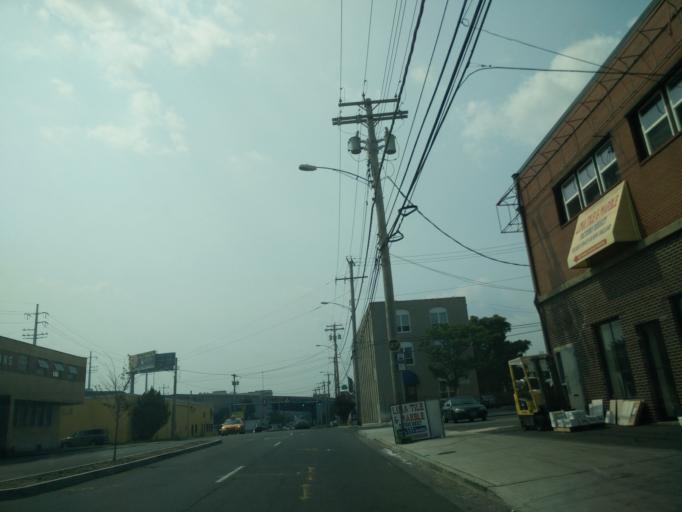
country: US
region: Connecticut
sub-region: Fairfield County
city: Bridgeport
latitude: 41.1683
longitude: -73.2171
